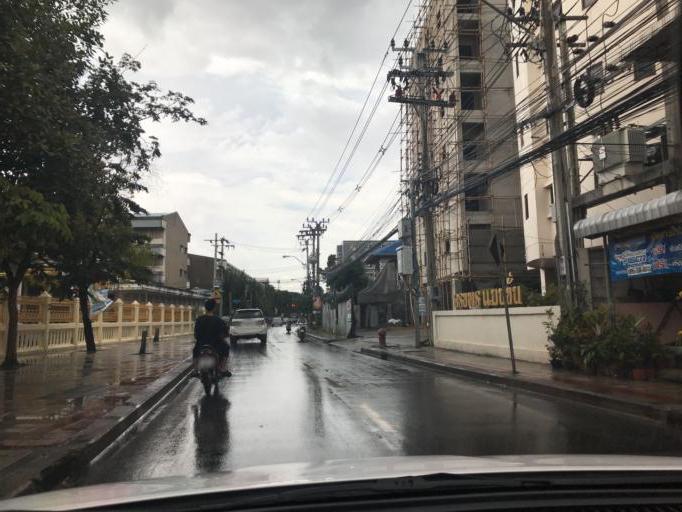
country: TH
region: Bangkok
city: Phasi Charoen
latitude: 13.7197
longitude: 100.4419
